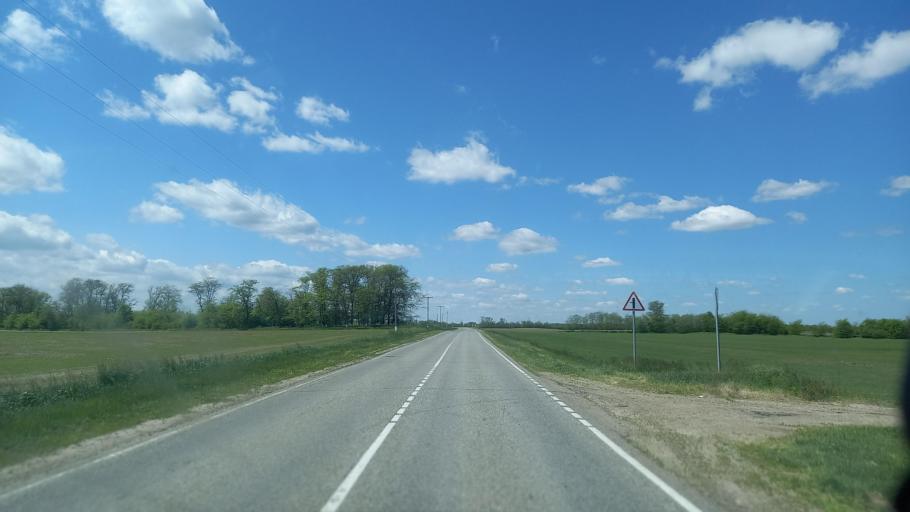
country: RU
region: Krasnodarskiy
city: Kazanskaya
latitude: 45.3491
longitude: 40.3401
